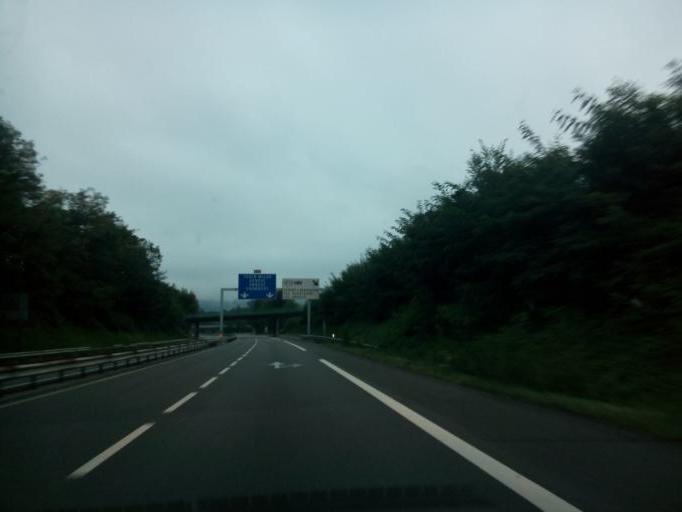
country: FR
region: Rhone-Alpes
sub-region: Departement de l'Isere
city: Chimilin
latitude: 45.5715
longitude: 5.5998
